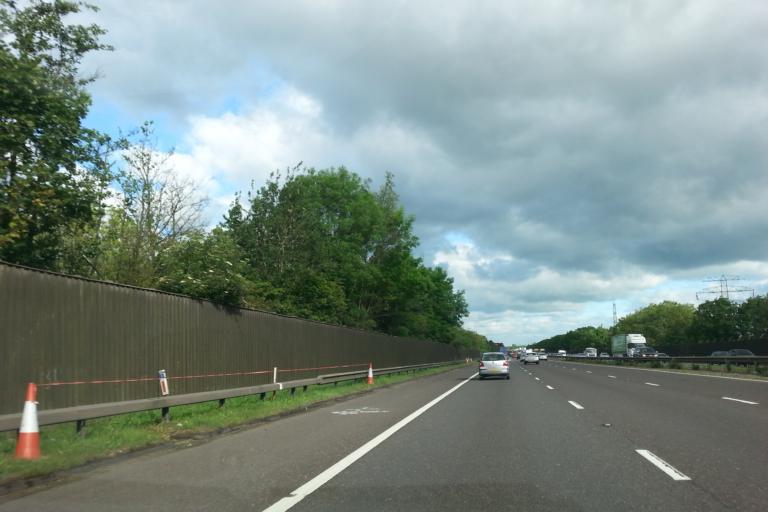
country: GB
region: England
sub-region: Warwickshire
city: Exhall
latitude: 52.4505
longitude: -1.4663
